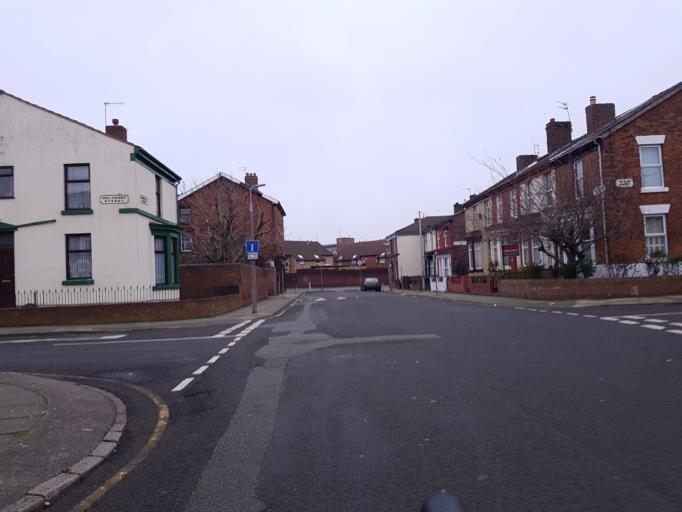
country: GB
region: England
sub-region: Liverpool
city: Liverpool
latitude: 53.4386
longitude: -2.9742
